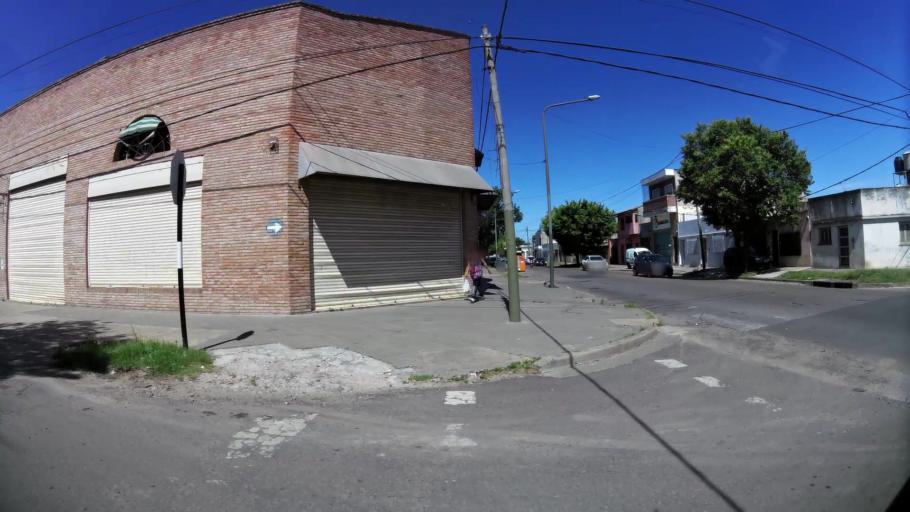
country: AR
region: Santa Fe
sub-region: Departamento de Rosario
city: Rosario
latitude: -32.9353
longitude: -60.6923
